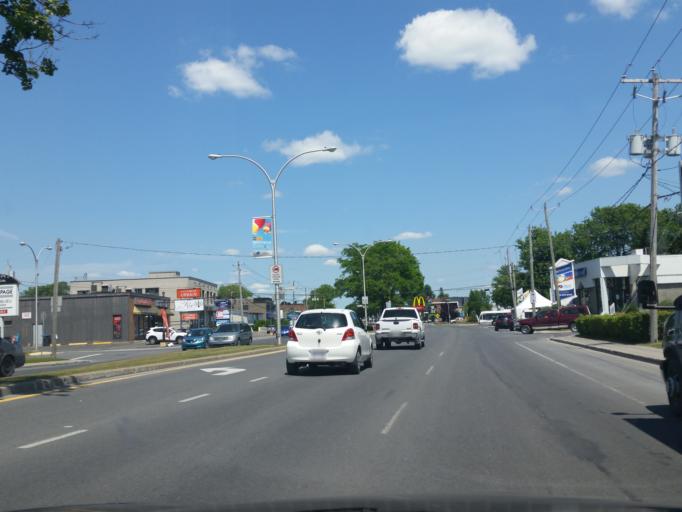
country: CA
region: Quebec
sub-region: Monteregie
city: Saint-Jean-sur-Richelieu
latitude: 45.3171
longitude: -73.2641
